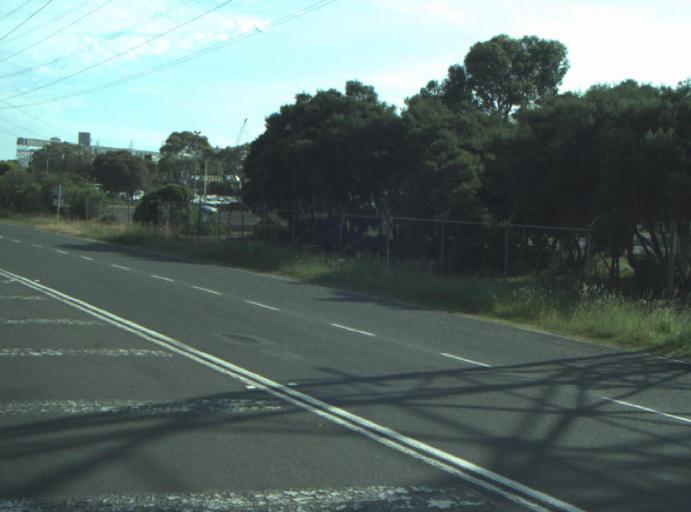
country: AU
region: Victoria
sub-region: Greater Geelong
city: East Geelong
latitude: -38.1383
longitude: 144.4199
